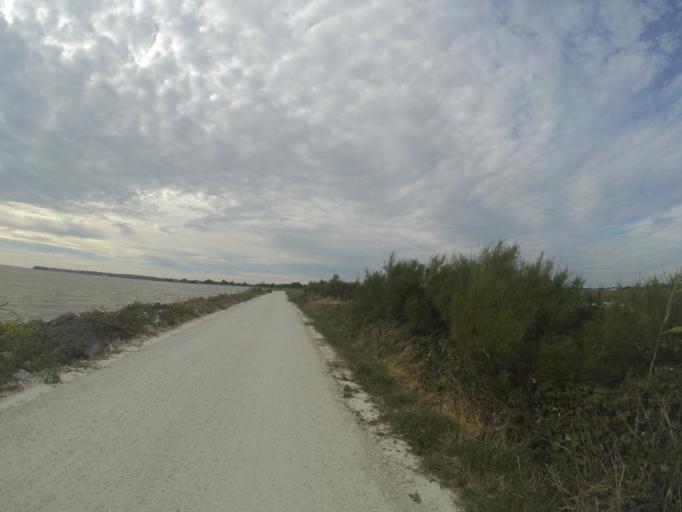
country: FR
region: Poitou-Charentes
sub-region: Departement de la Charente-Maritime
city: Meschers-sur-Gironde
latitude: 45.5468
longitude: -0.9124
